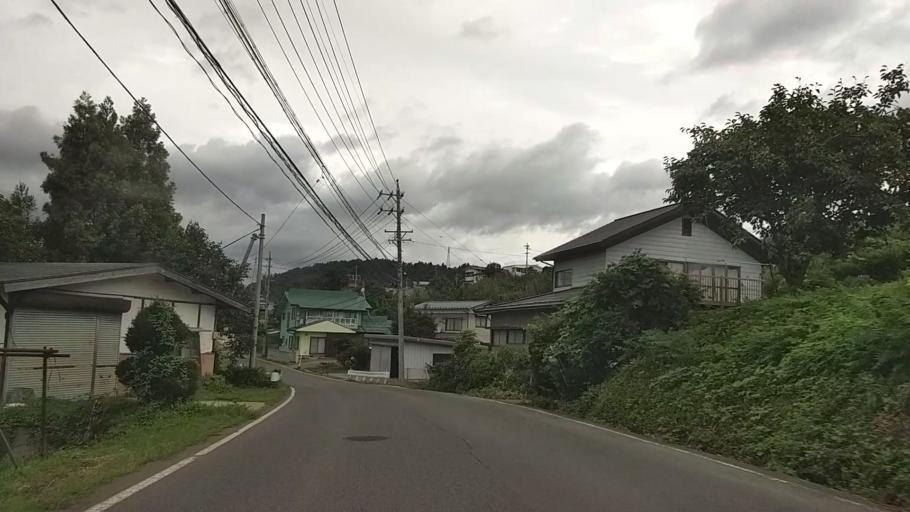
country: JP
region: Nagano
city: Iiyama
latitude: 36.8119
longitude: 138.3603
